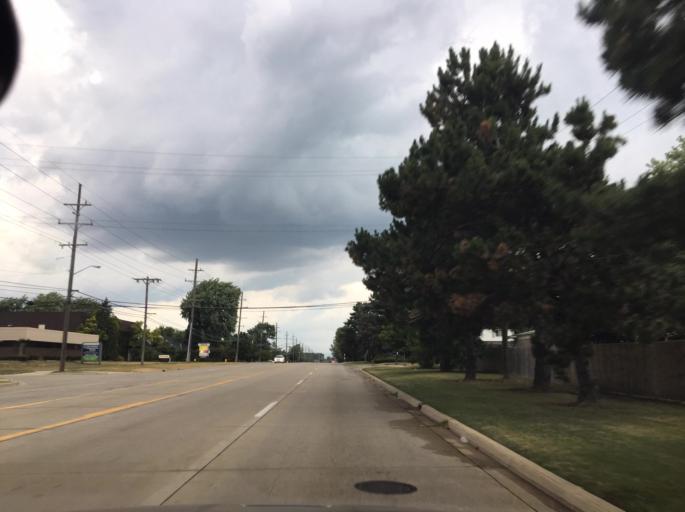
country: US
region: Michigan
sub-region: Macomb County
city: Fraser
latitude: 42.5569
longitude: -82.9504
